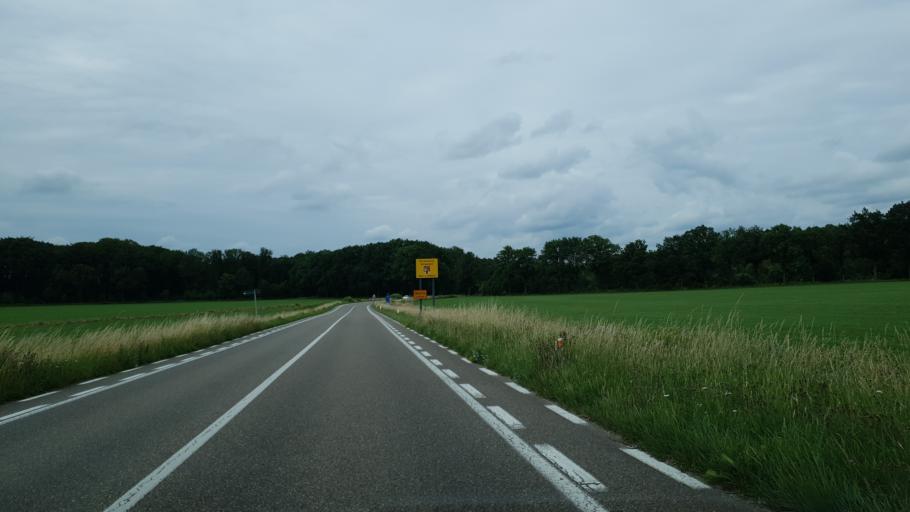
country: BE
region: Flanders
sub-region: Provincie Vlaams-Brabant
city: Scherpenheuvel-Zichem
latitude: 51.0356
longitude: 4.9826
